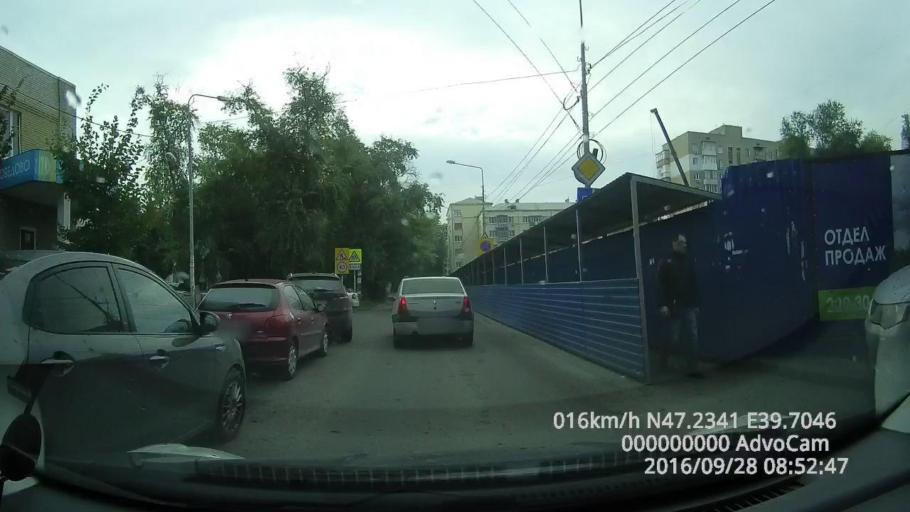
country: RU
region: Rostov
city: Rostov-na-Donu
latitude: 47.2339
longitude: 39.7047
